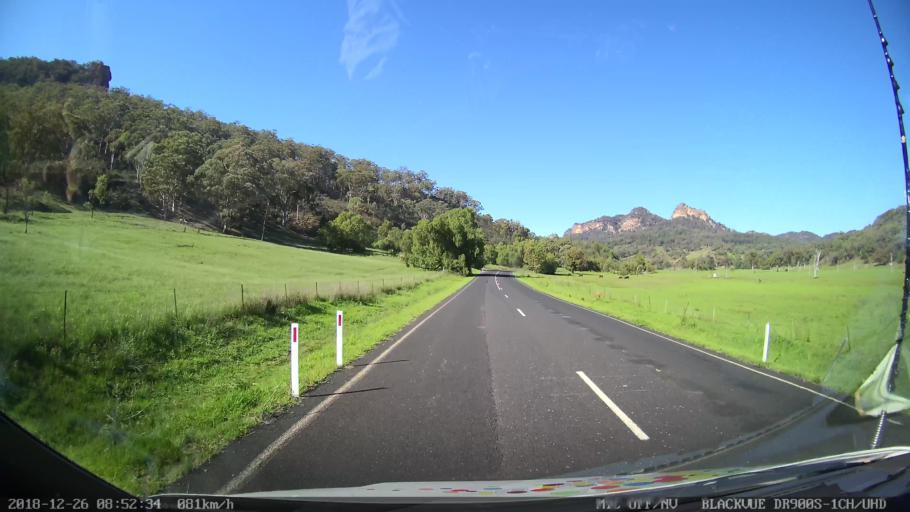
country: AU
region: New South Wales
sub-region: Mid-Western Regional
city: Kandos
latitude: -32.5979
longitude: 150.0856
